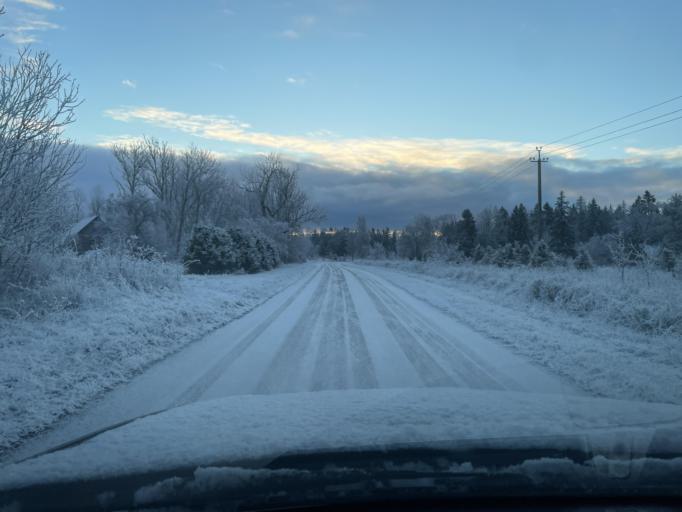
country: EE
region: Harju
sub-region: Keila linn
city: Keila
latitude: 59.3106
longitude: 24.2795
